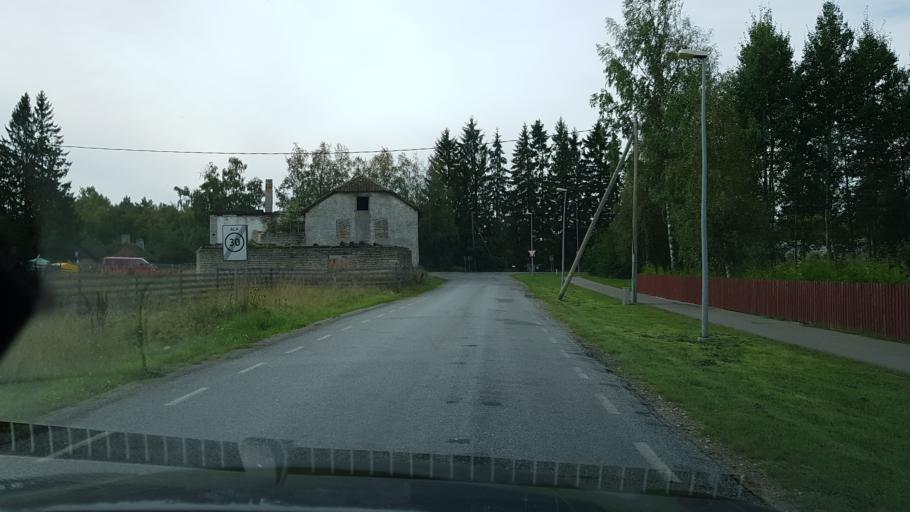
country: EE
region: Harju
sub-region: Raasiku vald
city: Raasiku
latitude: 59.4418
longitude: 25.1701
